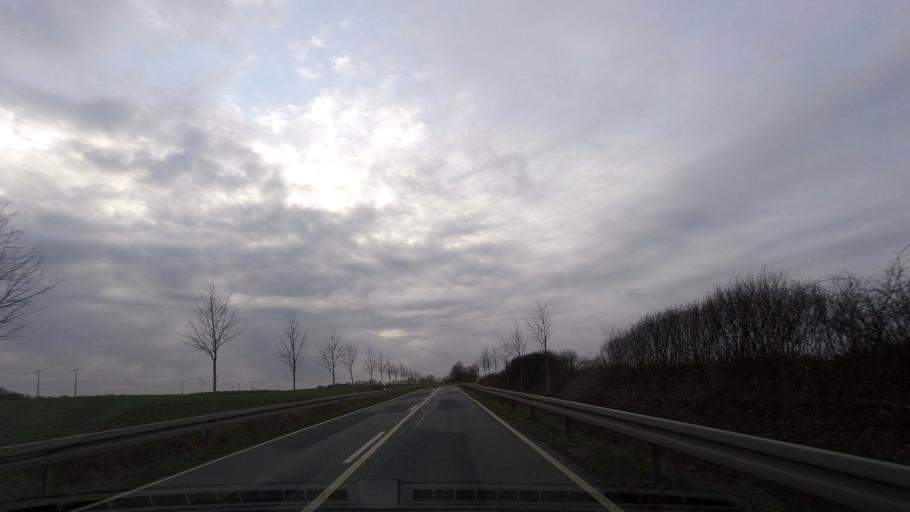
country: DE
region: Mecklenburg-Vorpommern
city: Robel
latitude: 53.3687
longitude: 12.5730
